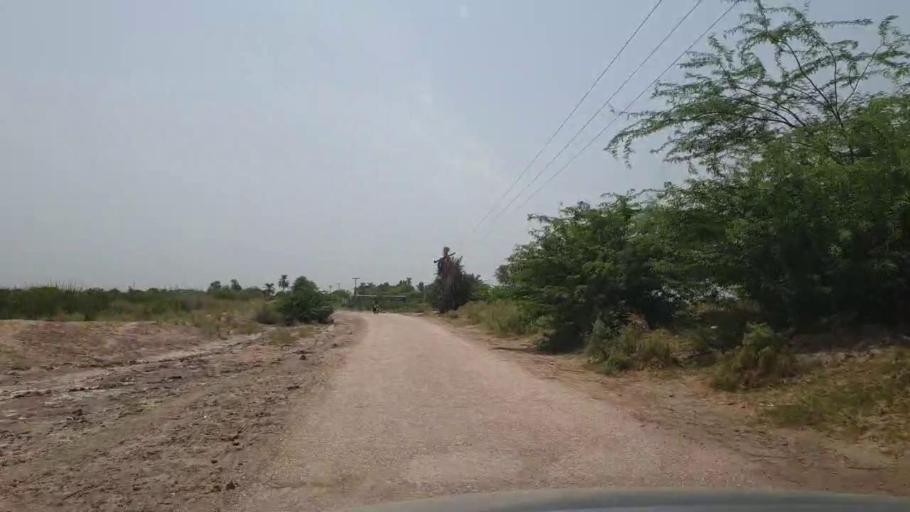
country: PK
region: Sindh
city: Garhi Yasin
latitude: 27.8808
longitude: 68.4952
